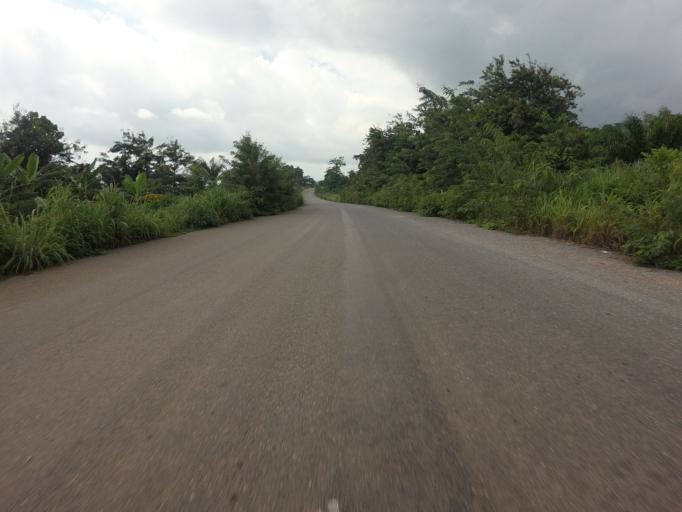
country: GH
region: Volta
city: Kpandu
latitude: 6.9078
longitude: 0.4450
